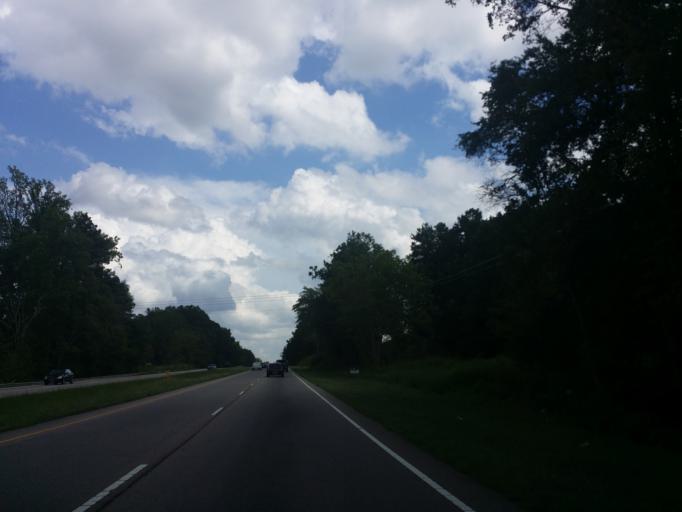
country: US
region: North Carolina
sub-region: Wake County
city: Morrisville
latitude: 35.9253
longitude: -78.8001
